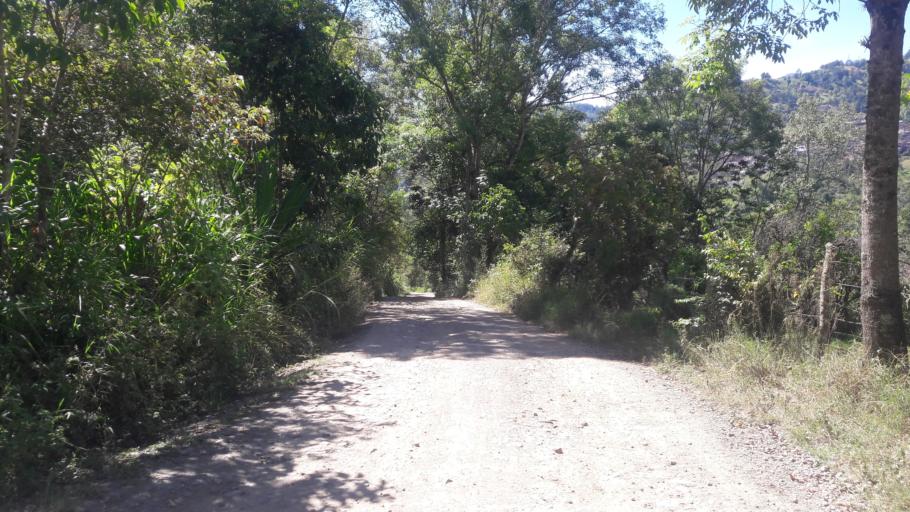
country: CO
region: Cundinamarca
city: Tenza
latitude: 5.0849
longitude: -73.4214
